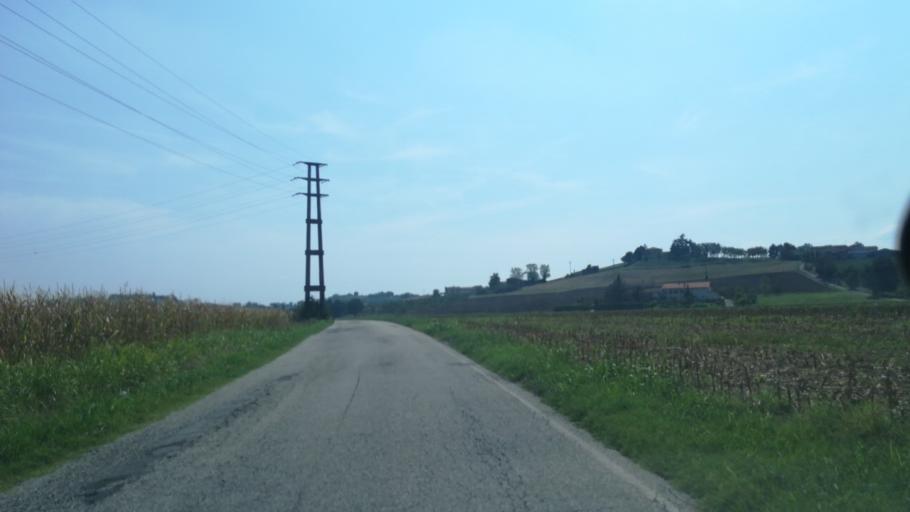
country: IT
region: Piedmont
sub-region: Provincia di Alessandria
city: San Giorgio Monferrato
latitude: 45.1078
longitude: 8.4414
